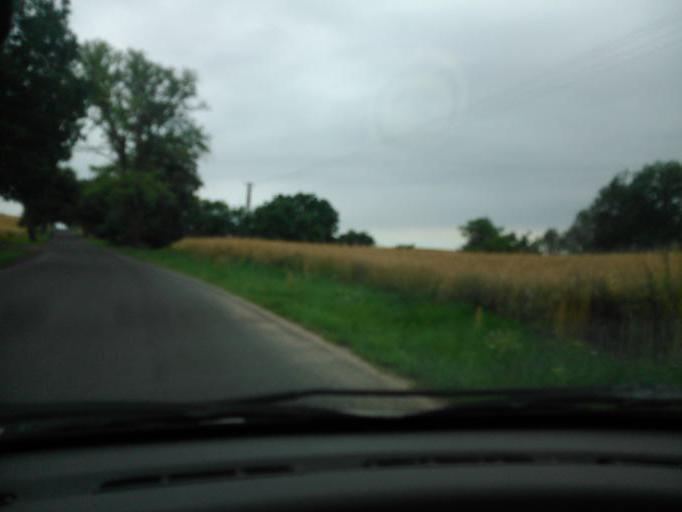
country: PL
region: Kujawsko-Pomorskie
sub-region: Powiat brodnicki
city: Jablonowo Pomorskie
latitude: 53.4128
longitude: 19.1342
